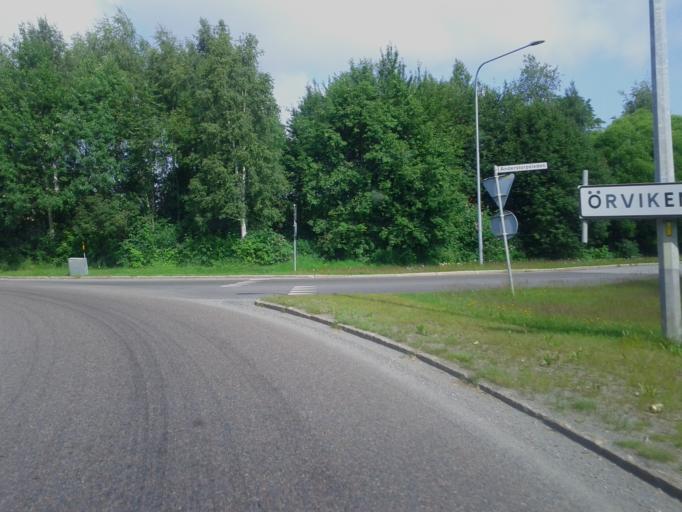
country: SE
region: Vaesterbotten
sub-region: Skelleftea Kommun
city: Skelleftea
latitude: 64.7432
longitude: 20.9618
